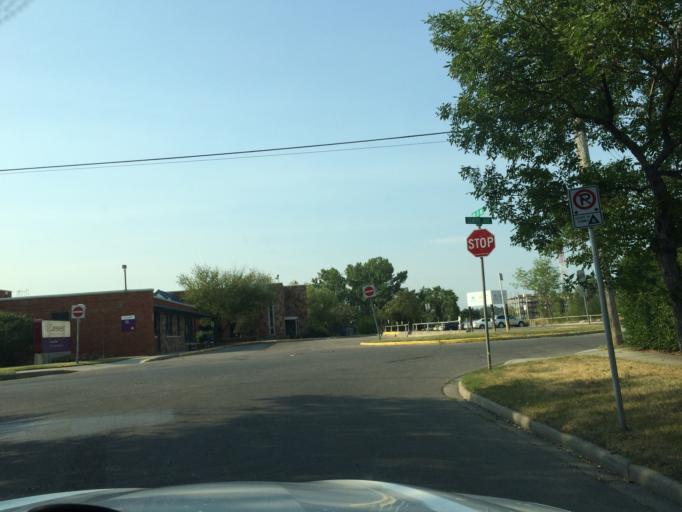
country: CA
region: Alberta
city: Calgary
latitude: 51.0526
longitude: -114.0378
